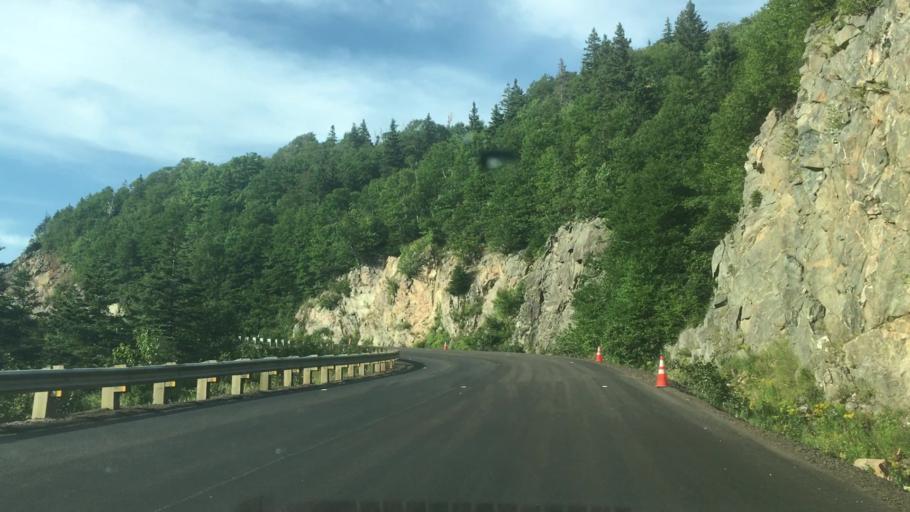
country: CA
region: Nova Scotia
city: Sydney Mines
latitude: 46.8193
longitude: -60.6527
